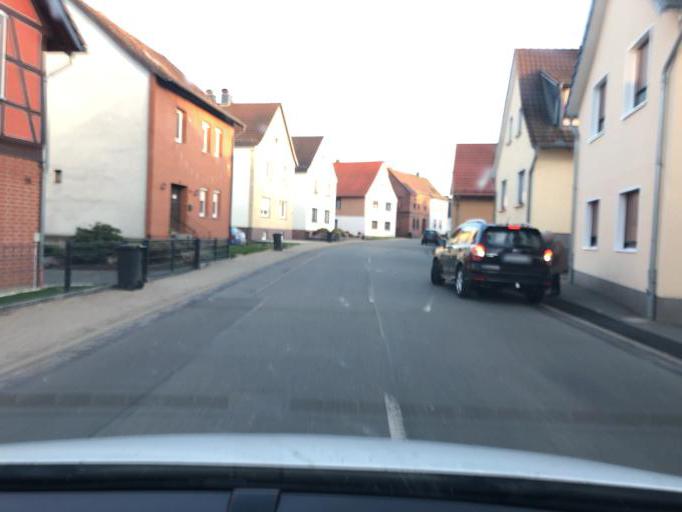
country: DE
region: Thuringia
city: Brehme
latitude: 51.5504
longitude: 10.3599
